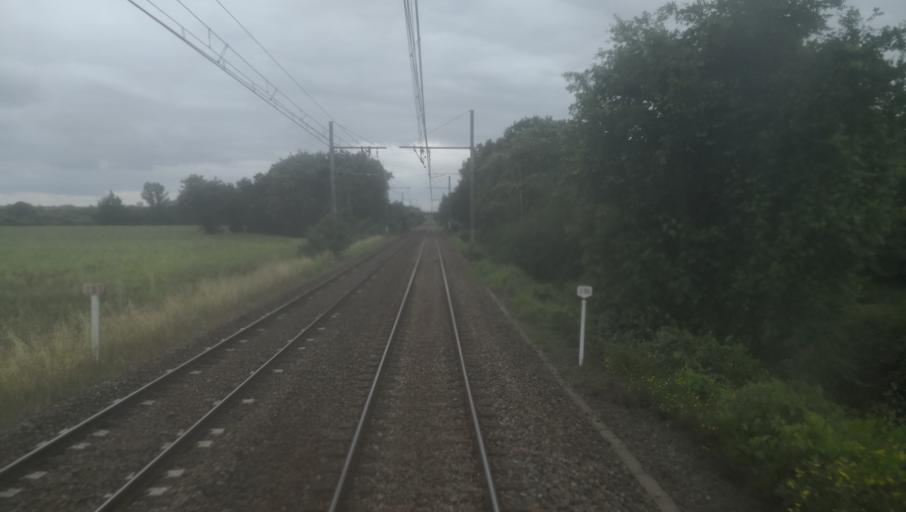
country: FR
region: Midi-Pyrenees
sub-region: Departement du Tarn-et-Garonne
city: Saint-Porquier
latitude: 44.0371
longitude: 1.1599
